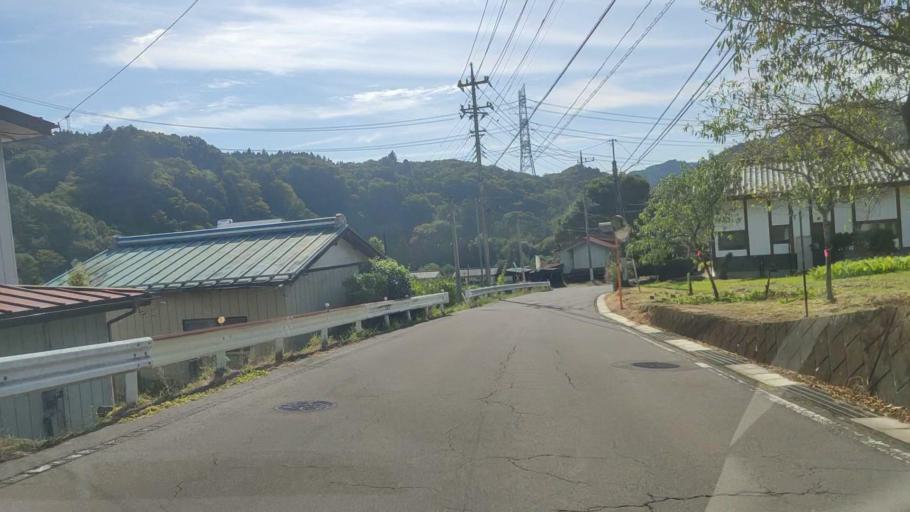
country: JP
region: Gunma
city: Nakanojomachi
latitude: 36.6196
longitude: 138.7792
